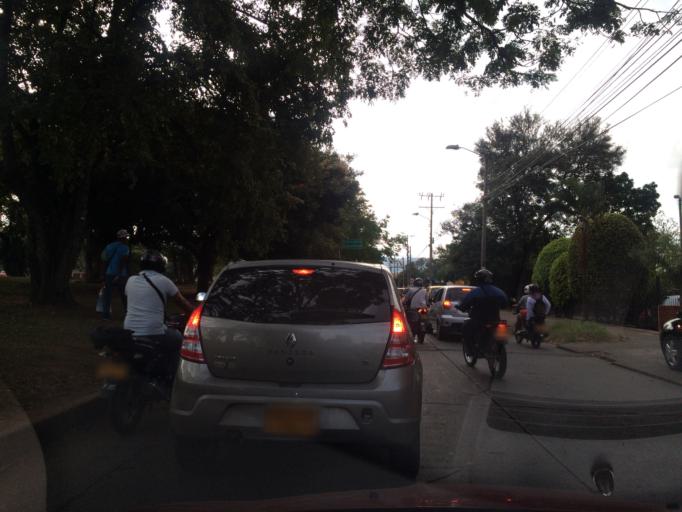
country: CO
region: Valle del Cauca
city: Cali
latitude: 3.3844
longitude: -76.5442
